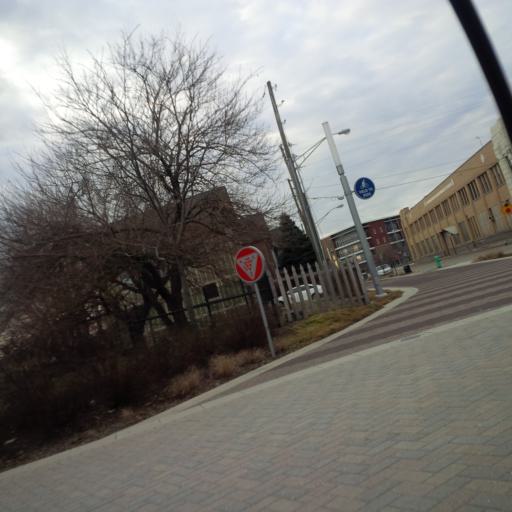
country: US
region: Indiana
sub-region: Marion County
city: Indianapolis
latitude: 39.7810
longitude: -86.1421
